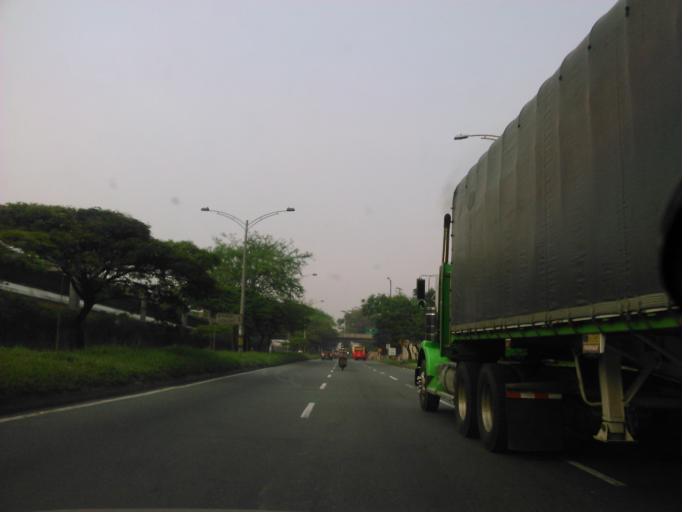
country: CO
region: Antioquia
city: Envigado
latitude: 6.1755
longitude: -75.5965
